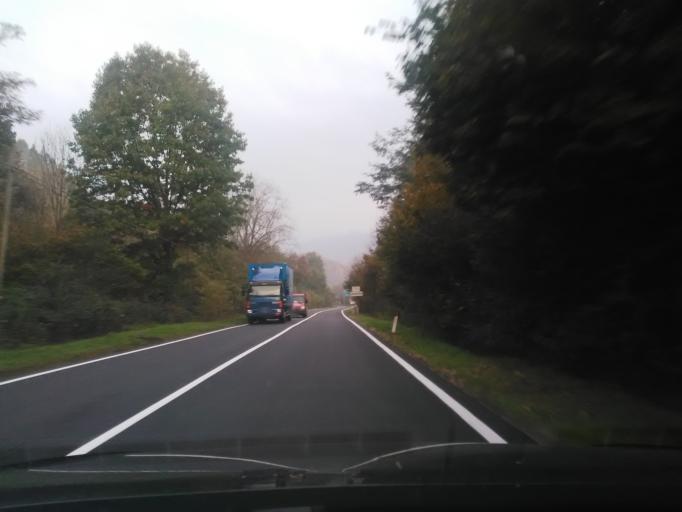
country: IT
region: Piedmont
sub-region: Provincia di Biella
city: Crevacuore
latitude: 45.6777
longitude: 8.2525
